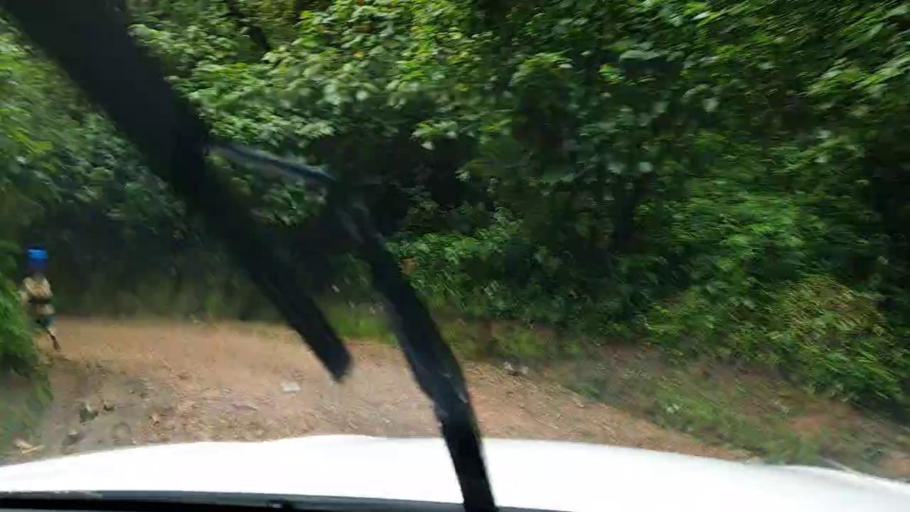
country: RW
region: Western Province
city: Cyangugu
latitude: -2.5588
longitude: 28.9827
